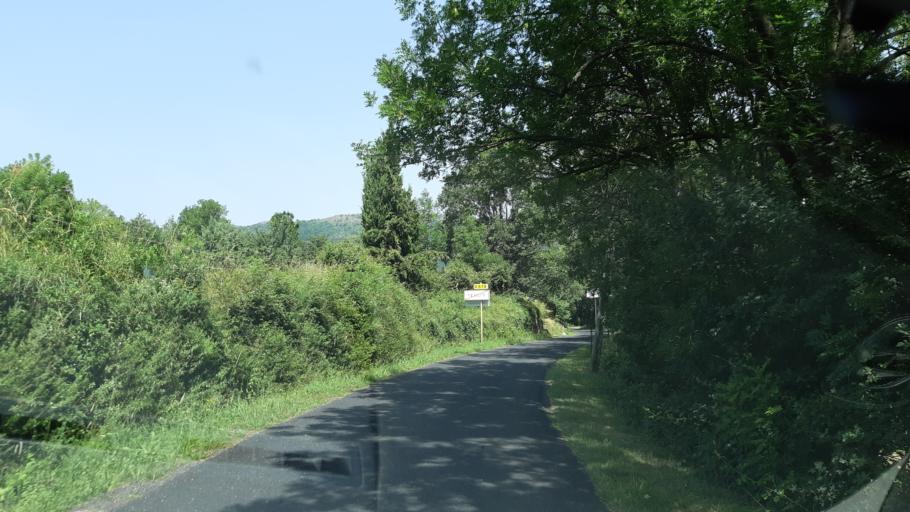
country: FR
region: Languedoc-Roussillon
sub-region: Departement des Pyrenees-Orientales
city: els Banys d'Arles
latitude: 42.5250
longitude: 2.6306
